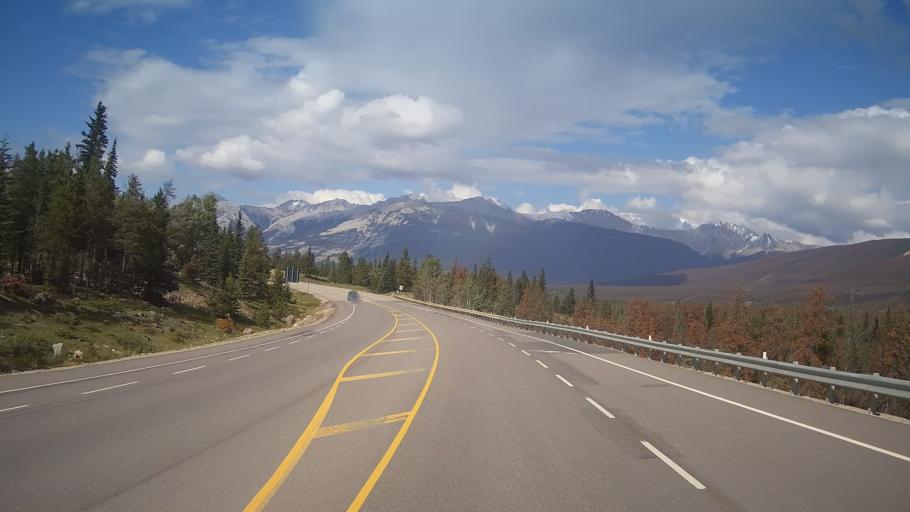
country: CA
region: Alberta
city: Jasper Park Lodge
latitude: 52.8704
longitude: -118.0737
